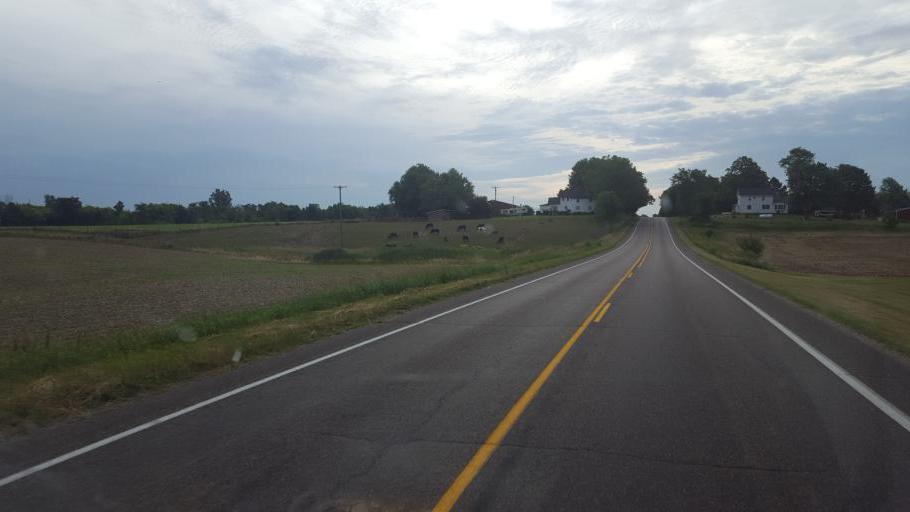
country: US
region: Michigan
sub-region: Eaton County
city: Charlotte
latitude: 42.6261
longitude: -84.8791
